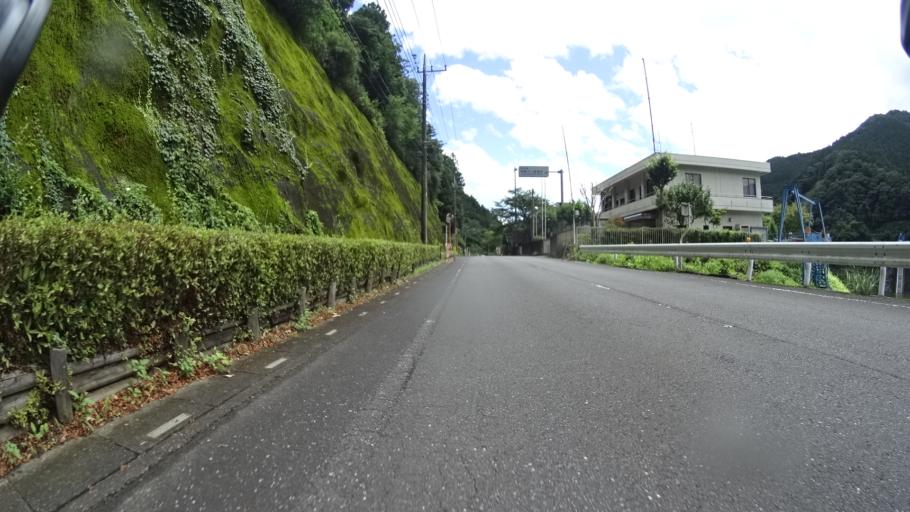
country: JP
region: Tokyo
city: Ome
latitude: 35.8752
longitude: 139.1751
